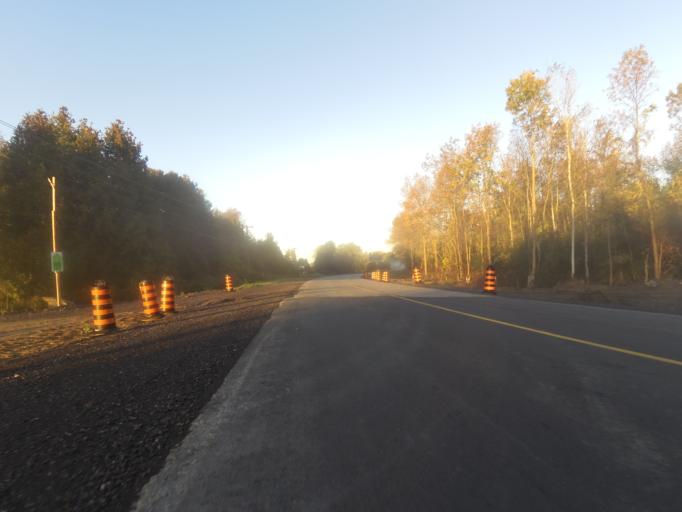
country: CA
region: Ontario
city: Quinte West
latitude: 44.0405
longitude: -77.6043
